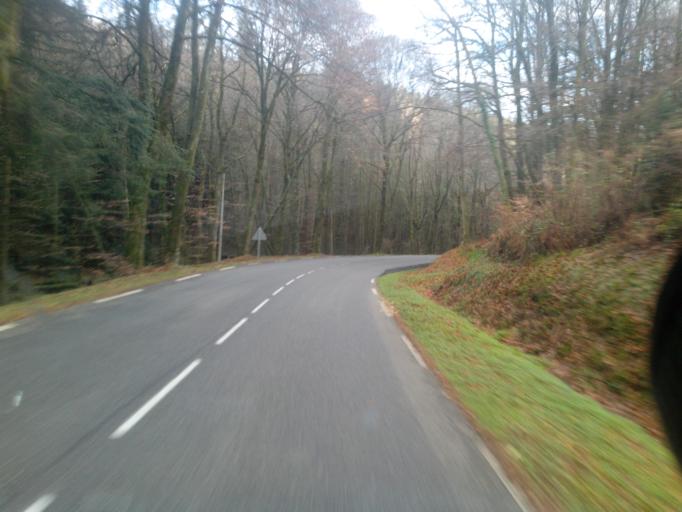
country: FR
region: Limousin
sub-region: Departement de la Haute-Vienne
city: Eymoutiers
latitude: 45.6671
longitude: 1.8045
